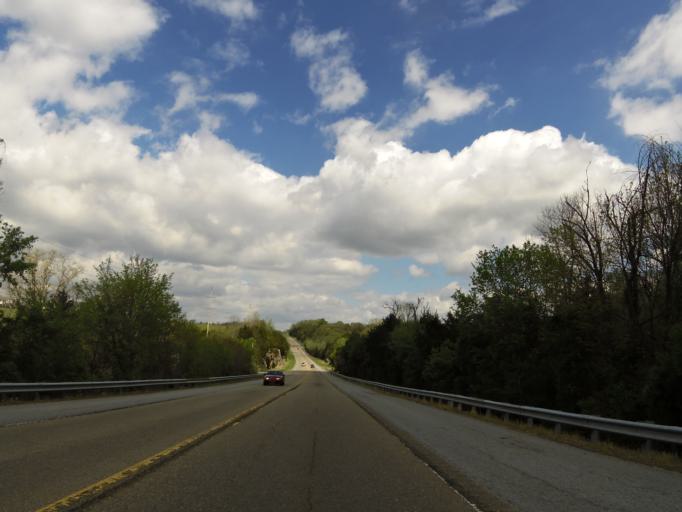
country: US
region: Tennessee
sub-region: Claiborne County
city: Harrogate
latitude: 36.5335
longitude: -83.6988
